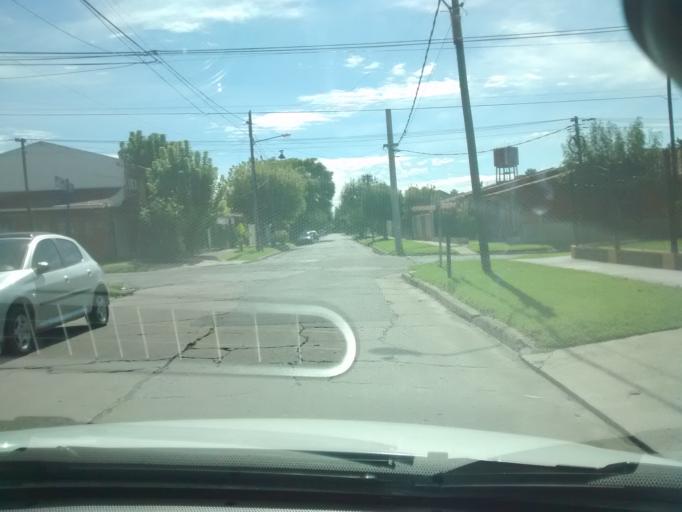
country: AR
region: Buenos Aires
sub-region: Partido de Moron
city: Moron
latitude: -34.6682
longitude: -58.6129
